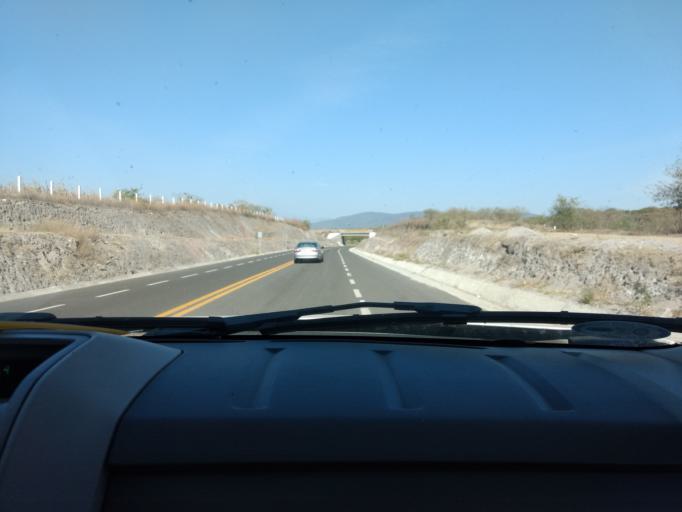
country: MX
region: Morelos
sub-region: Ayala
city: El Salitre
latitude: 18.6712
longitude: -98.9564
